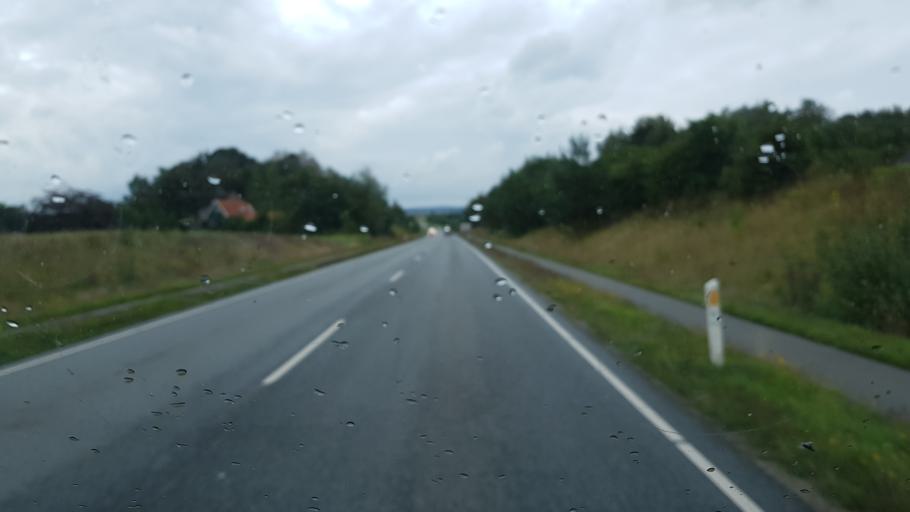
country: DK
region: Central Jutland
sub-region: Horsens Kommune
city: Horsens
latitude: 55.9008
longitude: 9.7476
